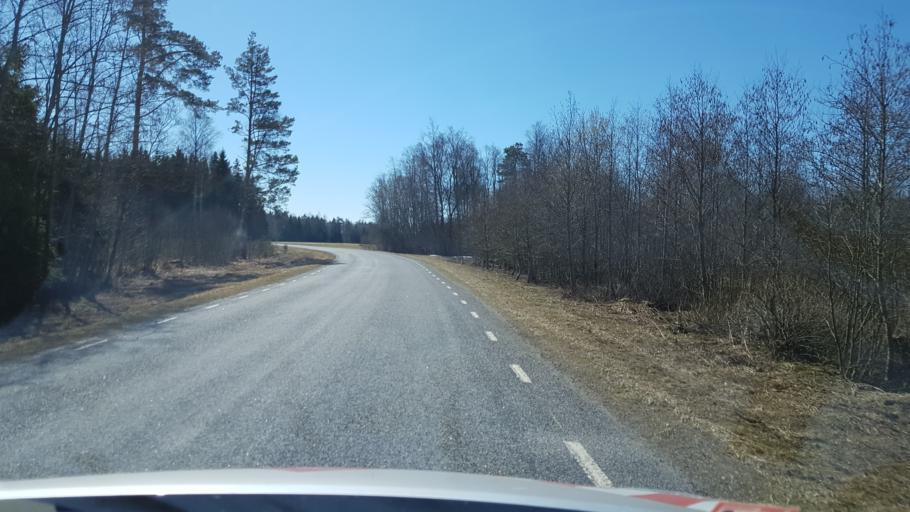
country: EE
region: Laeaene-Virumaa
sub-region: Haljala vald
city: Haljala
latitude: 59.4808
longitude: 26.2477
